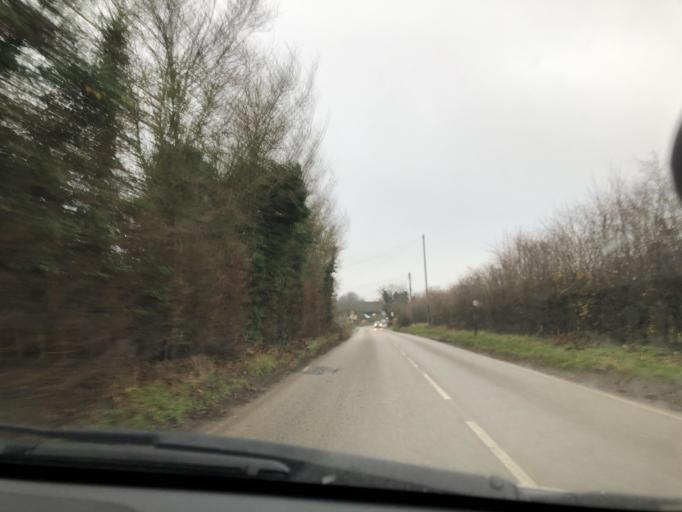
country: GB
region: England
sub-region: Kent
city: Longfield
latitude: 51.4111
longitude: 0.3299
